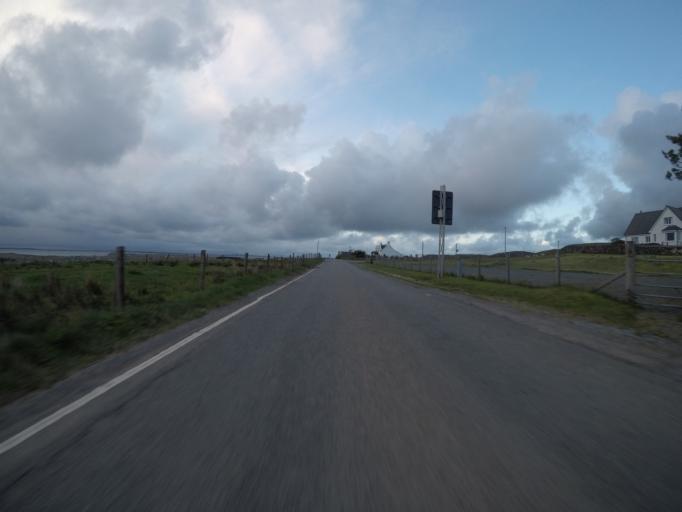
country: GB
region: Scotland
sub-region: Highland
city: Portree
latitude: 57.6365
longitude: -6.3764
